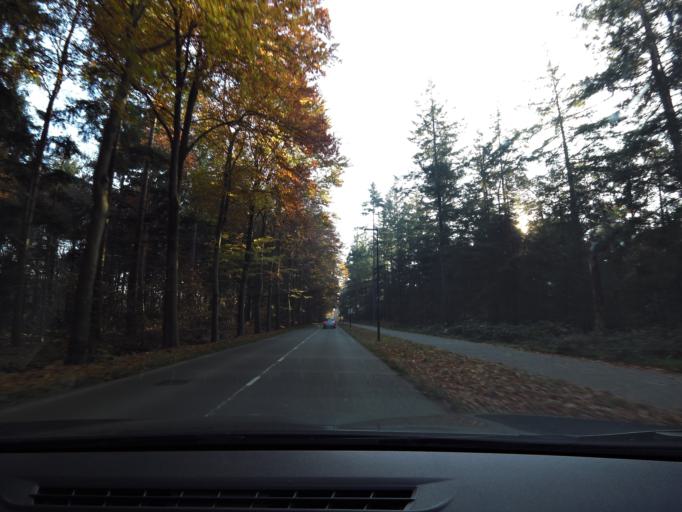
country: NL
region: North Brabant
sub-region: Gemeente Breda
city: Breda
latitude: 51.5475
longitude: 4.7777
